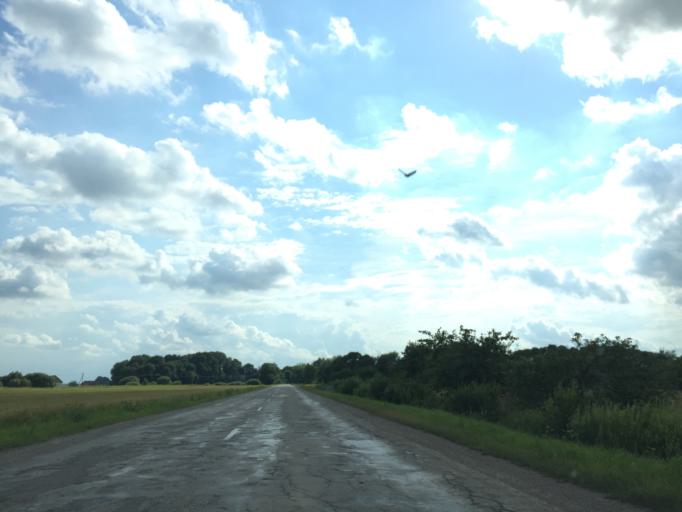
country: LV
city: Tervete
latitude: 56.5917
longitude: 23.4739
